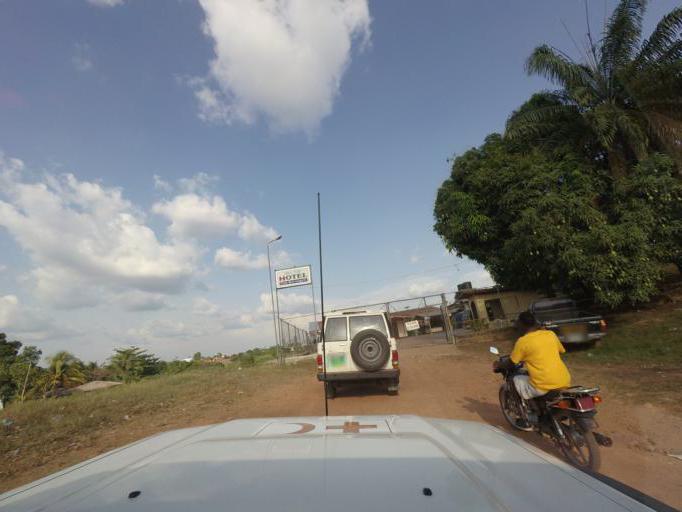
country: LR
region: Bong
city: Gbarnga
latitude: 6.9923
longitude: -9.4561
